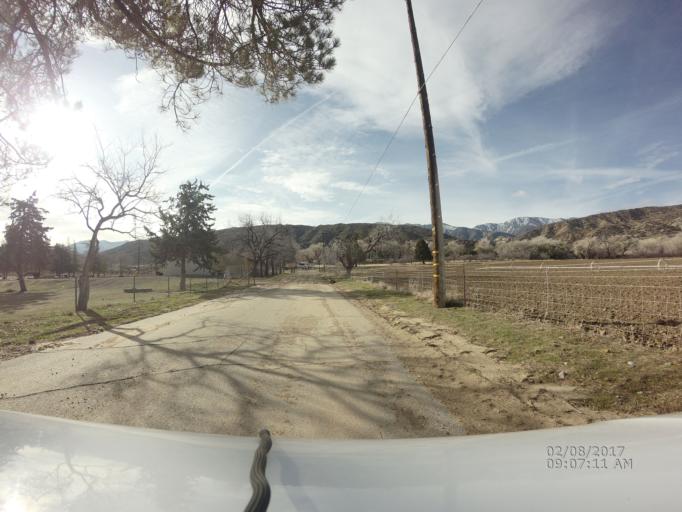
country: US
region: California
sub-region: Los Angeles County
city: Littlerock
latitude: 34.4441
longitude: -117.8528
